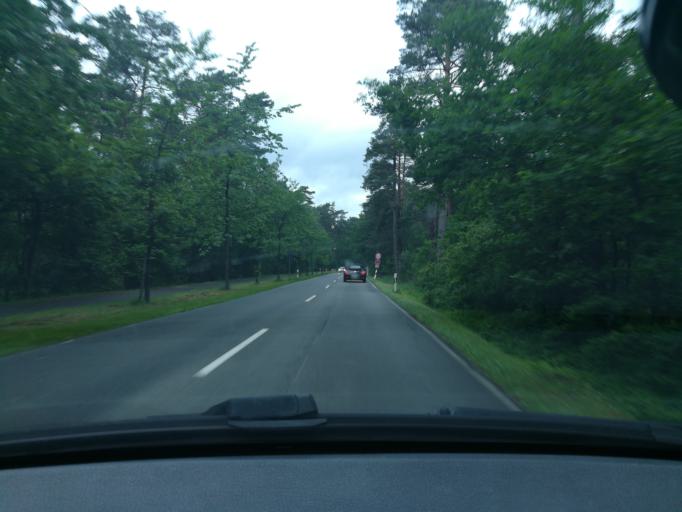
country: DE
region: North Rhine-Westphalia
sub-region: Regierungsbezirk Detmold
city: Oerlinghausen
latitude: 51.9214
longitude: 8.6554
